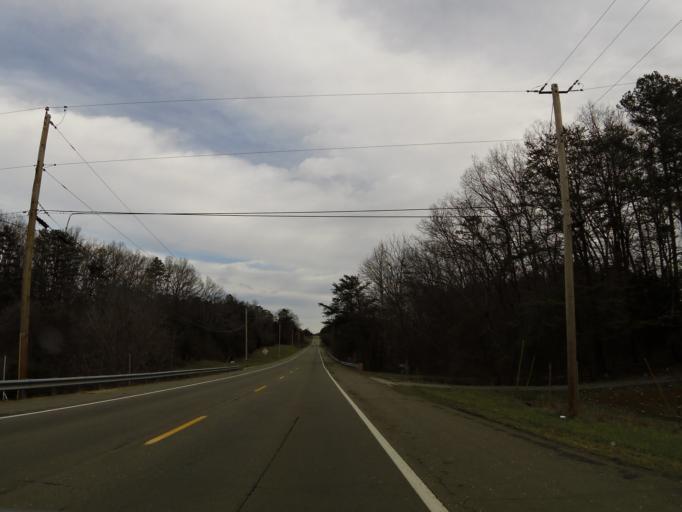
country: US
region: Tennessee
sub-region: Greene County
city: Mosheim
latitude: 36.0503
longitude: -82.9882
